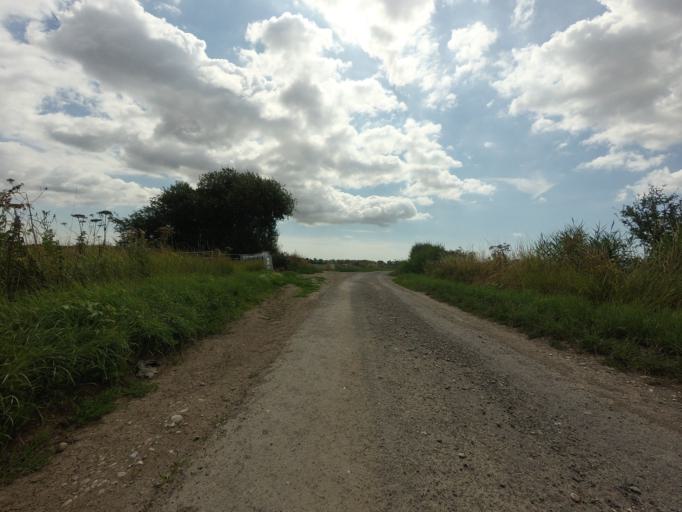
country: GB
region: England
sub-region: Kent
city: Stone
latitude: 51.0586
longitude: 0.7598
